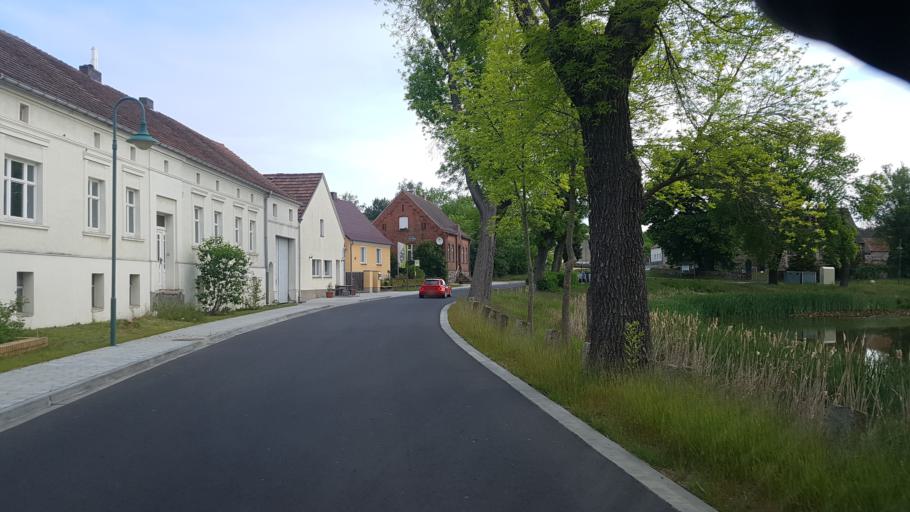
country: DE
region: Brandenburg
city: Baruth
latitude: 52.0100
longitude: 13.4691
